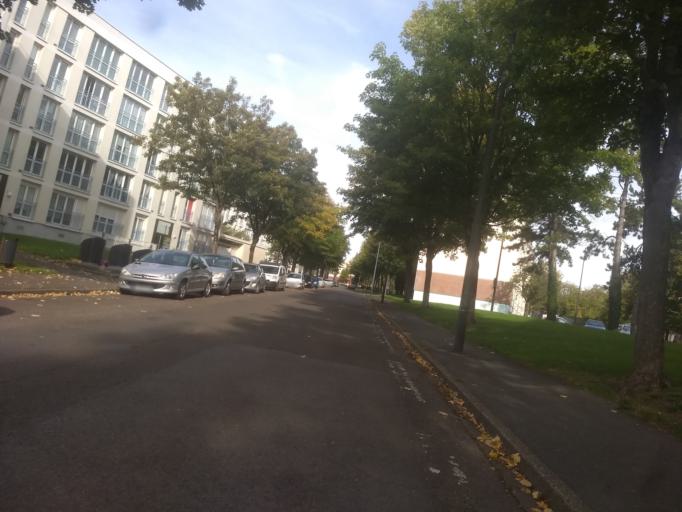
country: FR
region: Nord-Pas-de-Calais
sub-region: Departement du Pas-de-Calais
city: Achicourt
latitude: 50.2890
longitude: 2.7533
